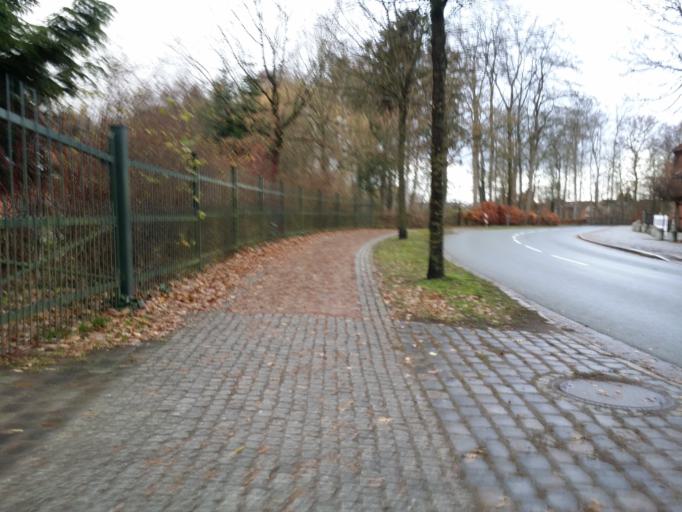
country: DE
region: Lower Saxony
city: Riede
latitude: 52.9852
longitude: 8.8762
